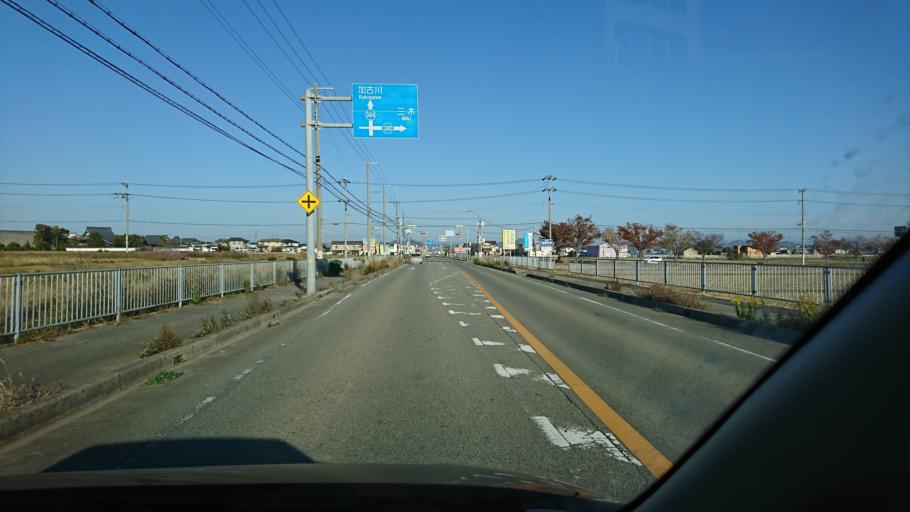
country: JP
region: Hyogo
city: Kakogawacho-honmachi
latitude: 34.7436
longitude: 134.9002
